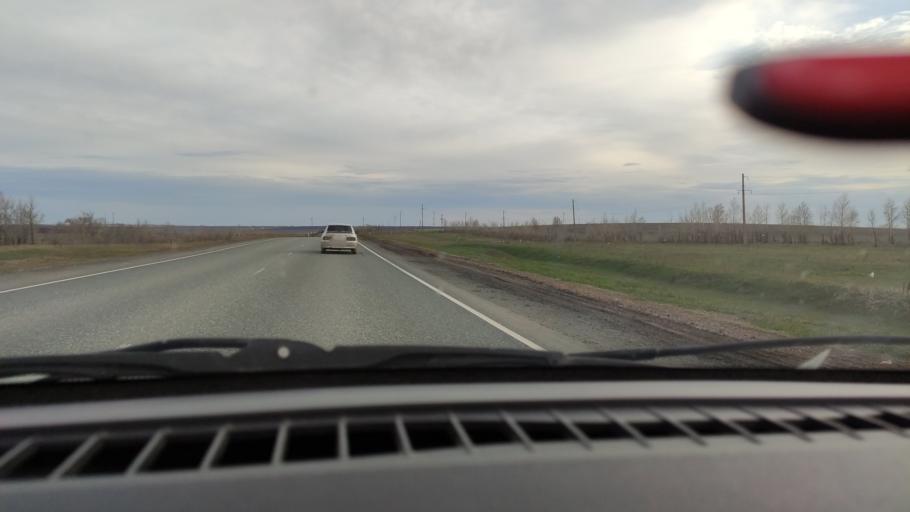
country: RU
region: Orenburg
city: Sakmara
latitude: 52.1302
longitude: 55.2811
